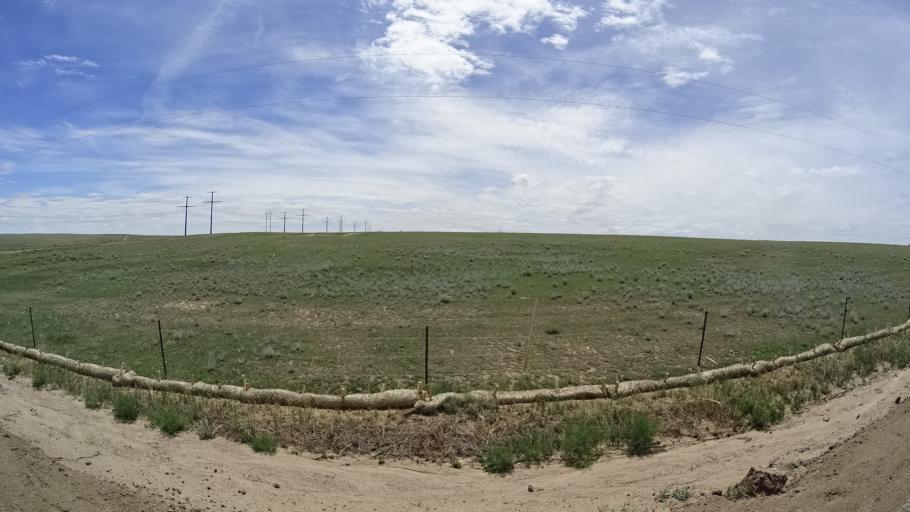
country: US
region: Colorado
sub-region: El Paso County
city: Fountain
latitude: 38.6940
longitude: -104.6301
